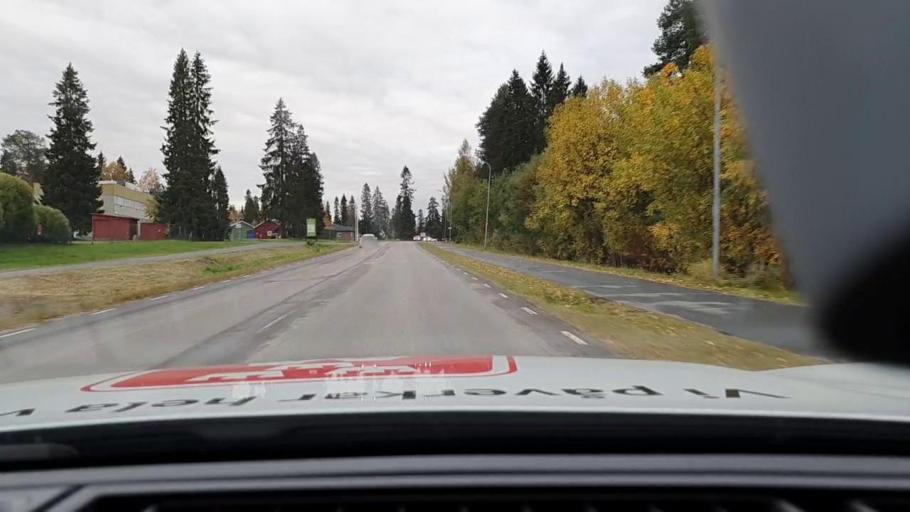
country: SE
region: Norrbotten
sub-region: Bodens Kommun
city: Boden
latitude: 65.8116
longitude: 21.6771
